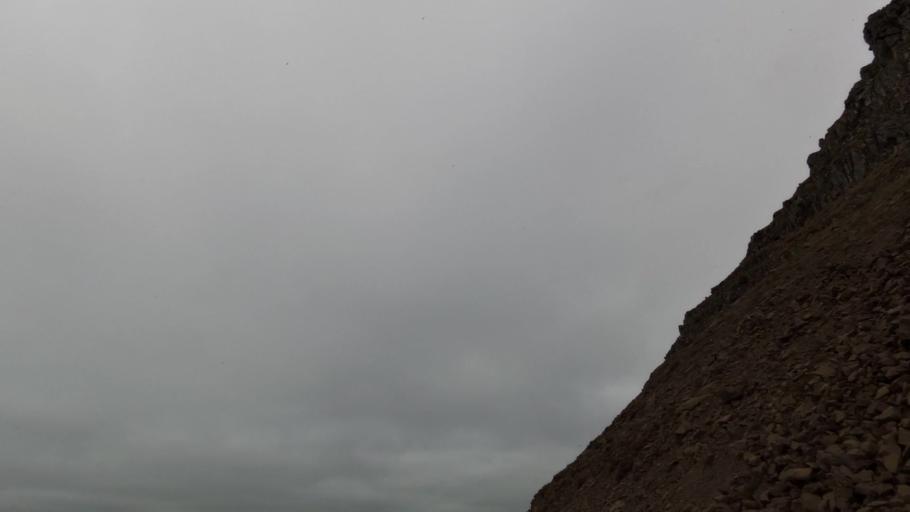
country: IS
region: West
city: Olafsvik
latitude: 65.5097
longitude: -24.5105
